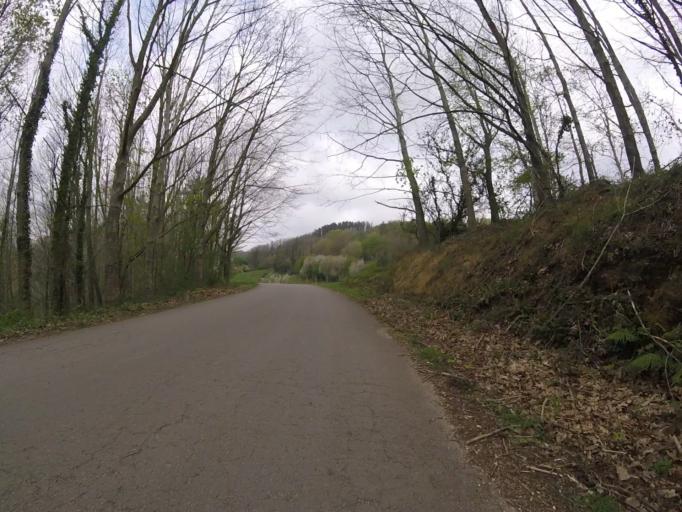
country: ES
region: Basque Country
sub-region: Provincia de Guipuzcoa
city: Zizurkil
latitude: 43.2095
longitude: -2.0779
